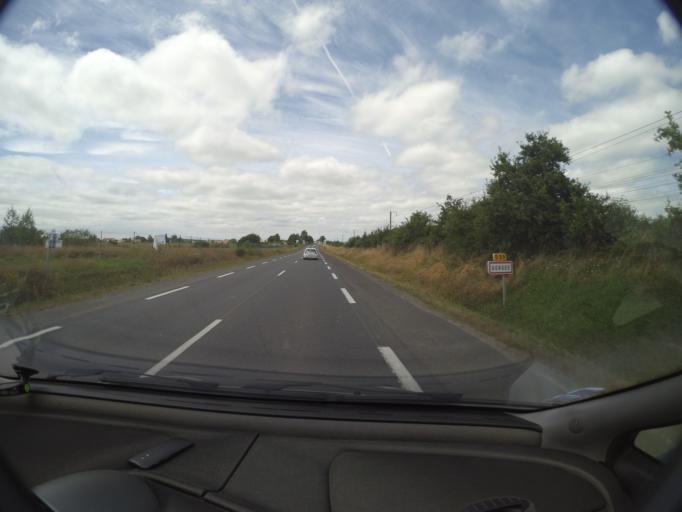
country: FR
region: Pays de la Loire
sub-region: Departement de la Loire-Atlantique
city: Gorges
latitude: 47.0978
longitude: -1.3032
